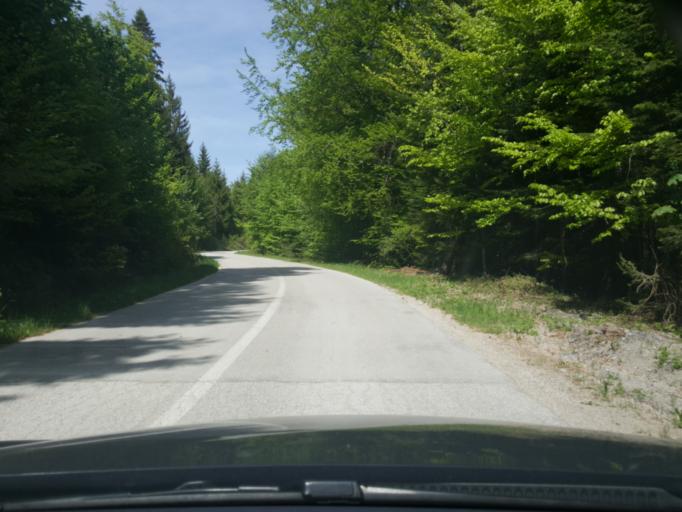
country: RS
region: Central Serbia
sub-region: Zlatiborski Okrug
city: Bajina Basta
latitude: 43.9102
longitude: 19.5017
